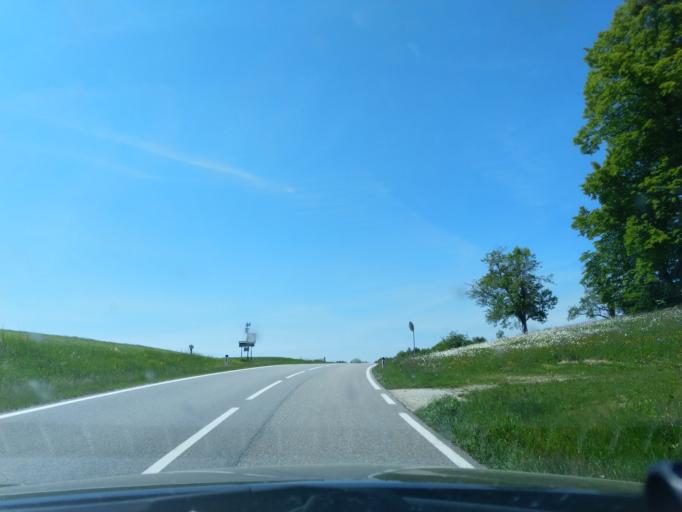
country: AT
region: Upper Austria
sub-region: Politischer Bezirk Ried im Innkreis
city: Ried im Innkreis
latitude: 48.2537
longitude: 13.4332
